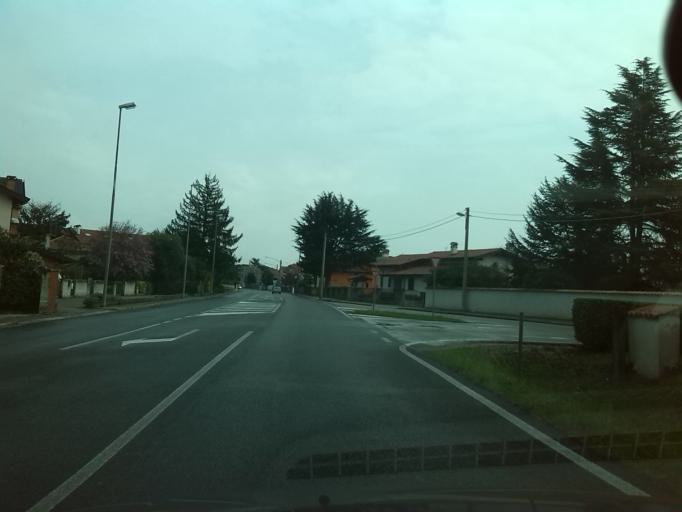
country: IT
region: Friuli Venezia Giulia
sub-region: Provincia di Gorizia
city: Mossa
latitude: 45.9354
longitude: 13.5646
